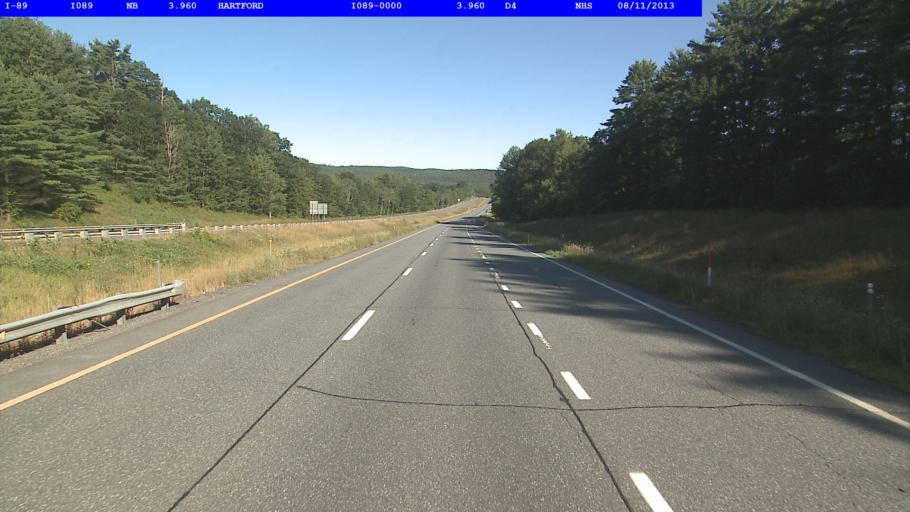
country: US
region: Vermont
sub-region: Windsor County
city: White River Junction
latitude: 43.6671
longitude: -72.3856
